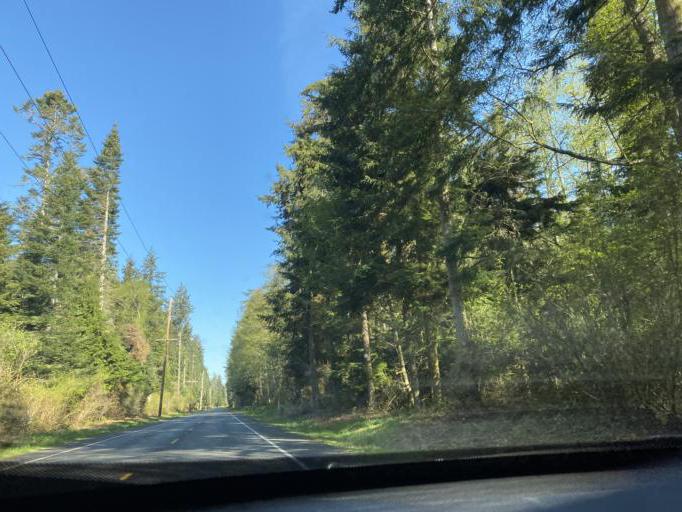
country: US
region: Washington
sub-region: Island County
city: Freeland
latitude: 48.0666
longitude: -122.5999
